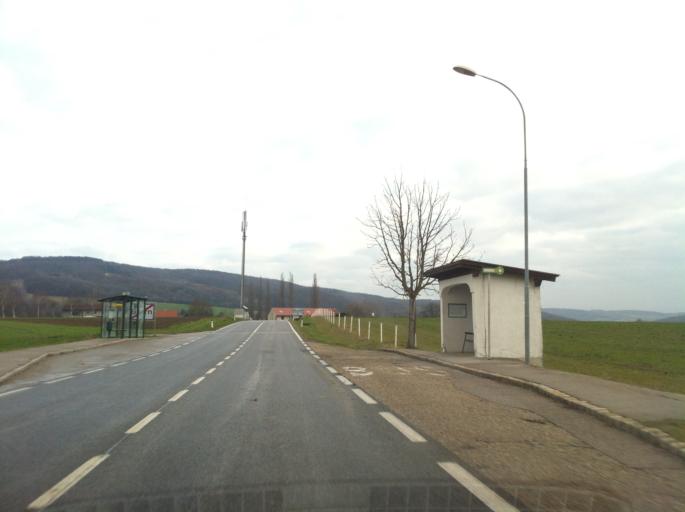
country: AT
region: Lower Austria
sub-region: Politischer Bezirk Tulln
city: Tulbing
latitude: 48.2605
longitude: 16.0742
